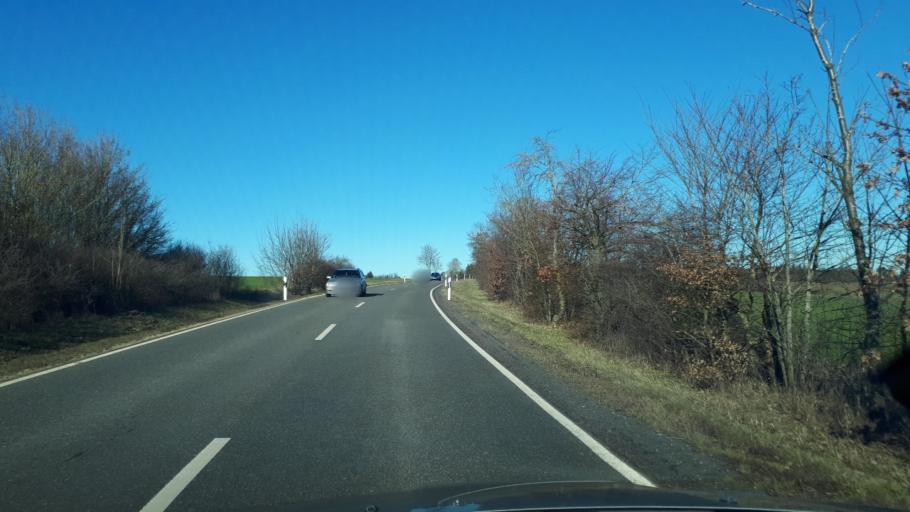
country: DE
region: Rheinland-Pfalz
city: Ellscheid
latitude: 50.1478
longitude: 6.9291
